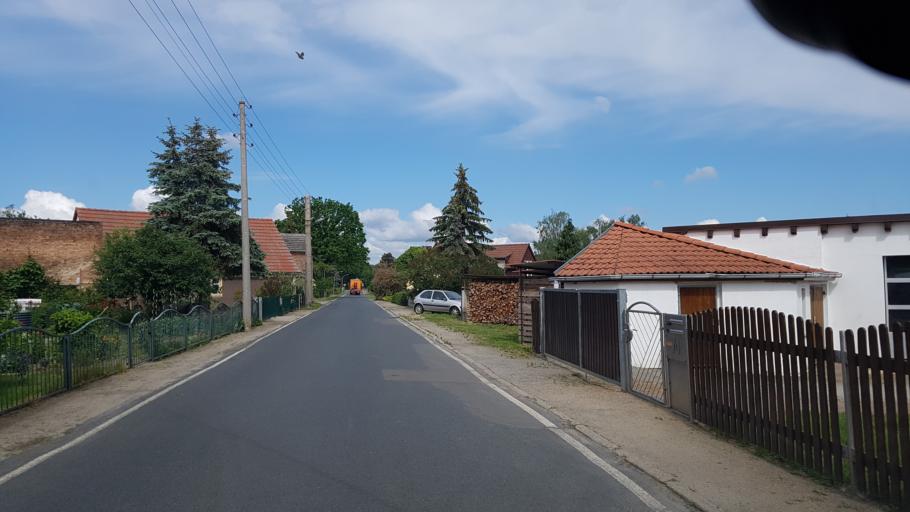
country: DE
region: Brandenburg
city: Luckau
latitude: 51.8210
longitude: 13.6924
